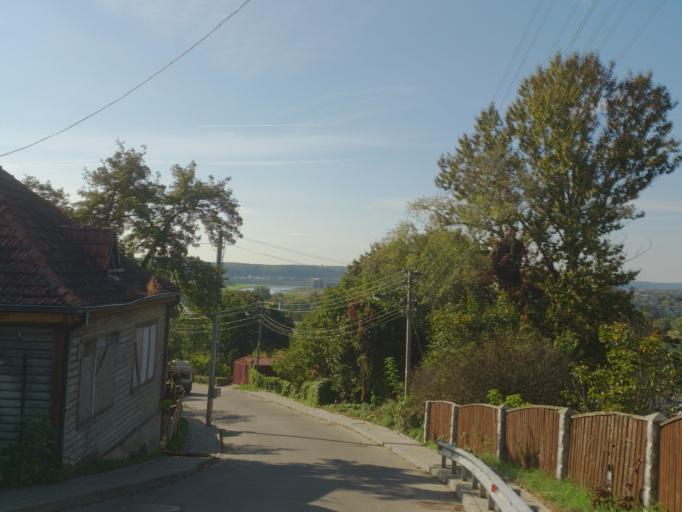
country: LT
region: Kauno apskritis
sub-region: Kaunas
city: Kaunas
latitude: 54.9047
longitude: 23.9040
